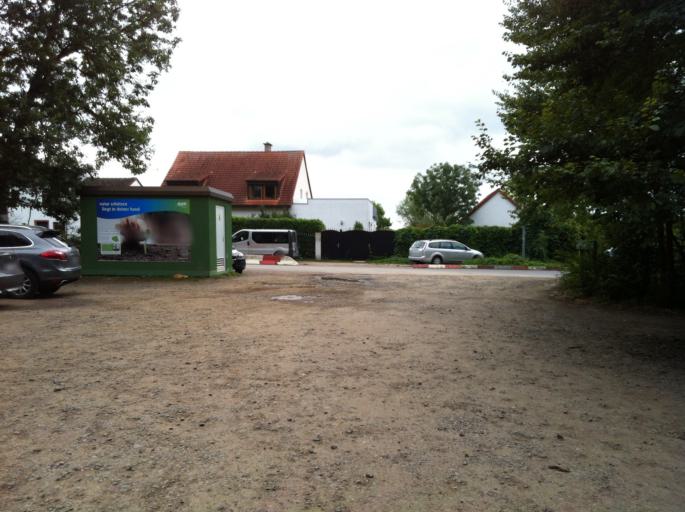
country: DE
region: Rheinland-Pfalz
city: Ober-Olm
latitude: 49.9526
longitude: 8.1834
